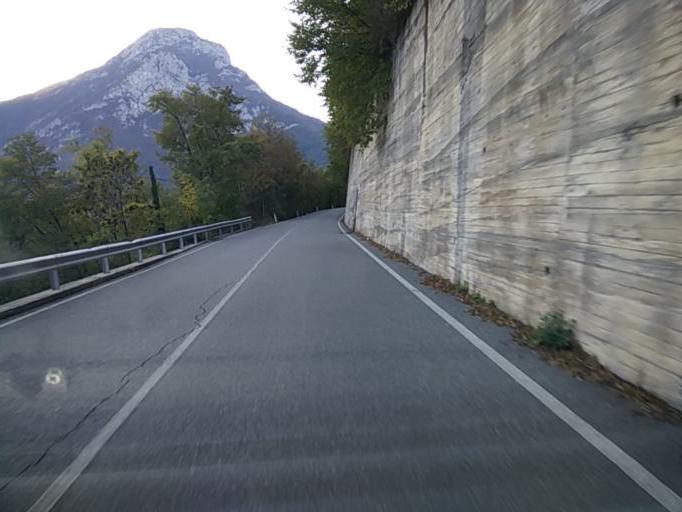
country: IT
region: Lombardy
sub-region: Provincia di Brescia
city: Gargnano
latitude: 45.6817
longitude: 10.6287
